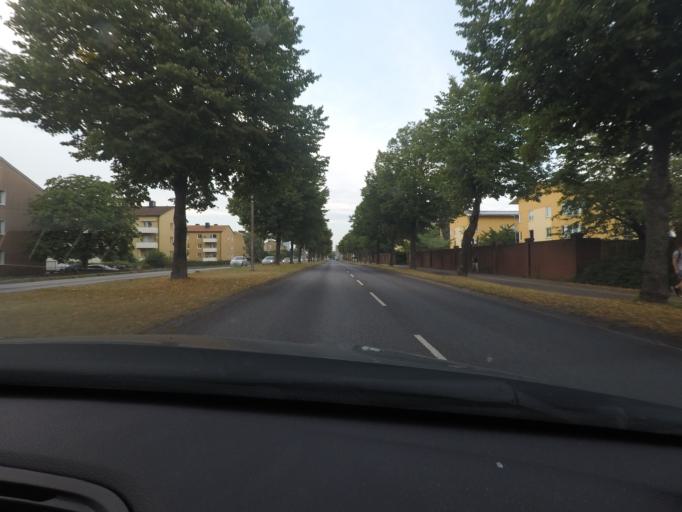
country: SE
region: Halland
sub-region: Halmstads Kommun
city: Halmstad
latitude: 56.6664
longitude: 12.8779
